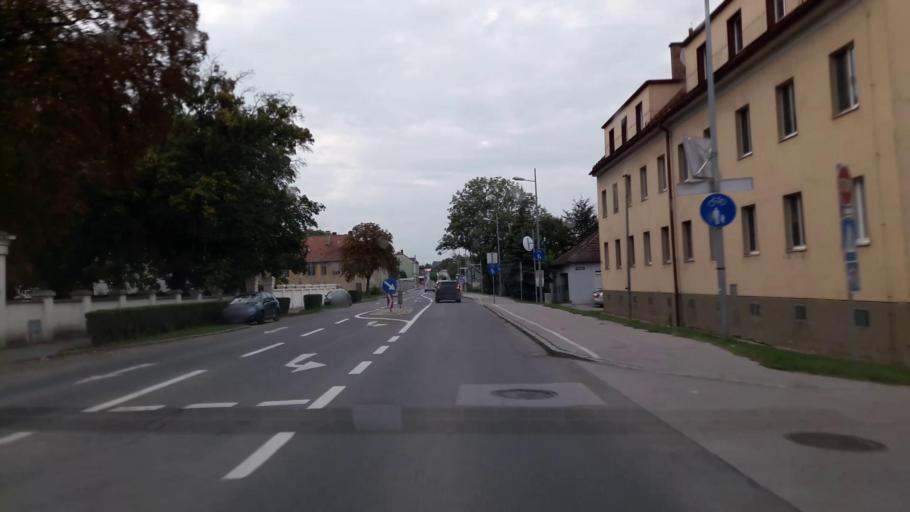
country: AT
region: Lower Austria
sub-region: Politischer Bezirk Wien-Umgebung
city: Schwadorf
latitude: 48.0696
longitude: 16.5860
